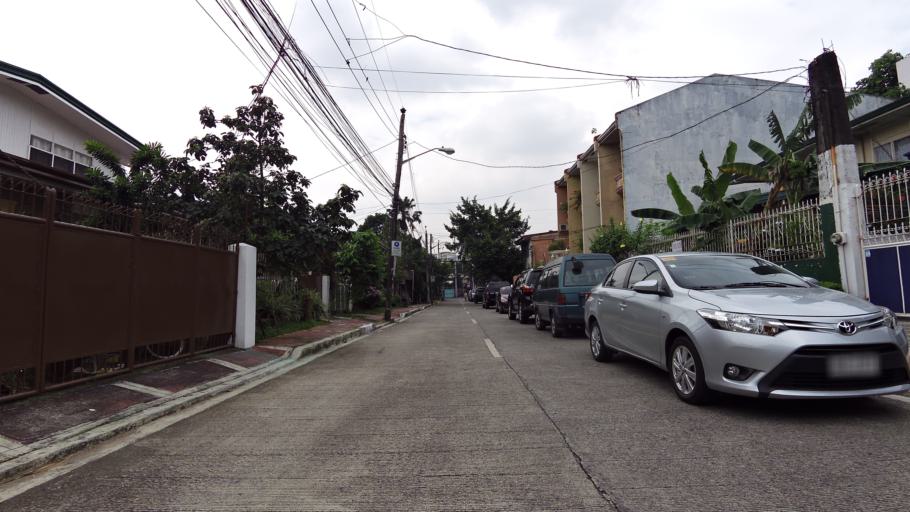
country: PH
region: Metro Manila
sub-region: Quezon City
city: Quezon City
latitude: 14.6375
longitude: 121.0590
